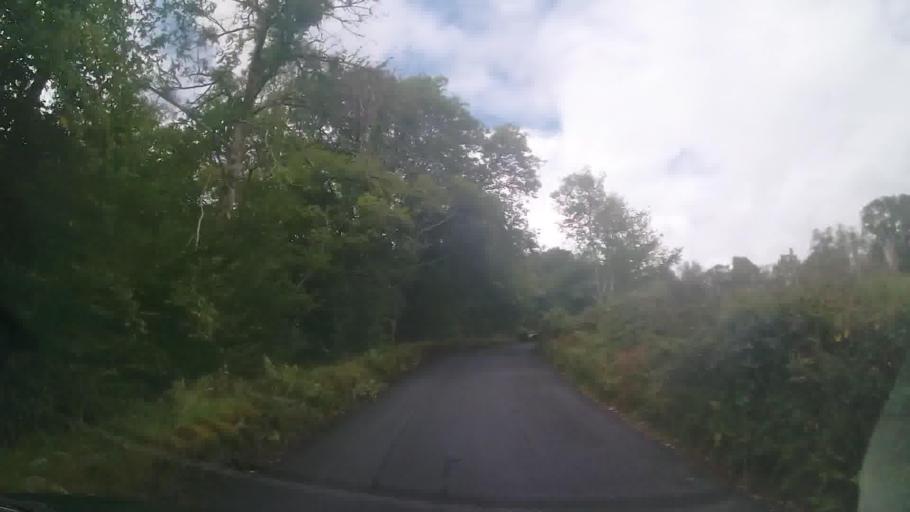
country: GB
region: England
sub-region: Cumbria
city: Ambleside
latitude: 54.4193
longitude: -3.0347
